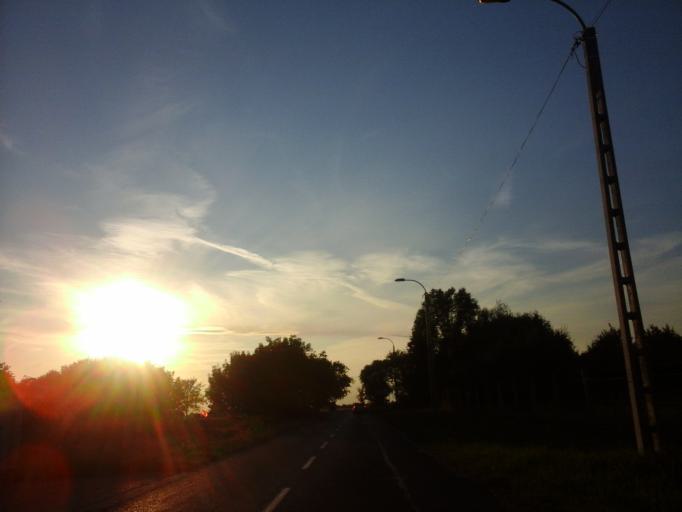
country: HU
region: Hajdu-Bihar
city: Hajduszoboszlo
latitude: 47.4586
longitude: 21.3987
